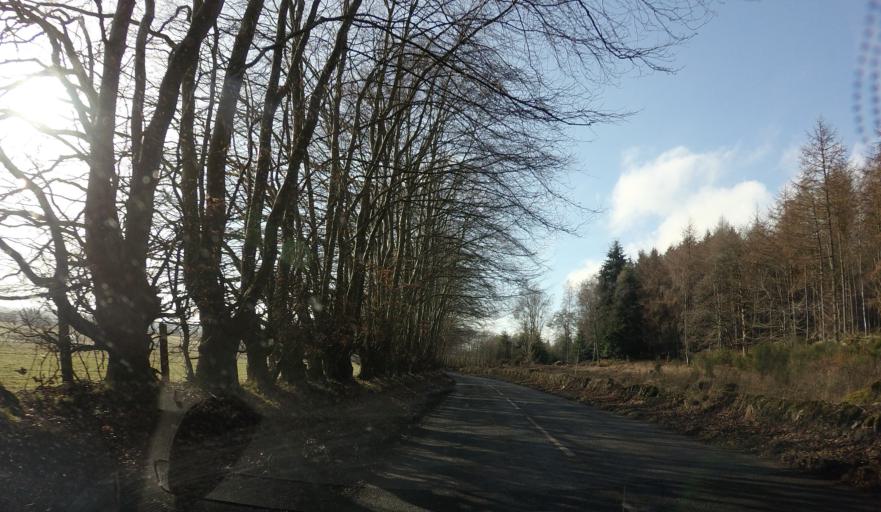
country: GB
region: Scotland
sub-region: Perth and Kinross
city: Bankfoot
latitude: 56.5708
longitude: -3.5998
